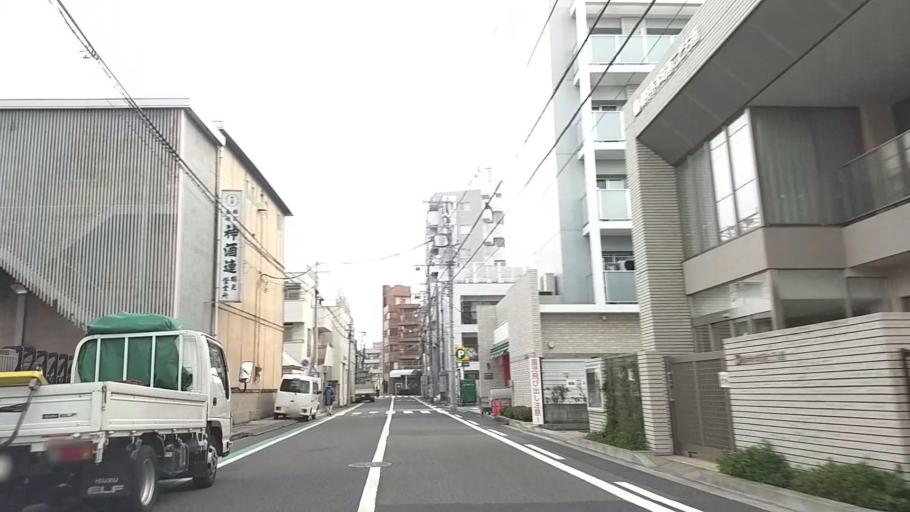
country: JP
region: Kanagawa
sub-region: Kawasaki-shi
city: Kawasaki
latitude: 35.5025
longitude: 139.6800
